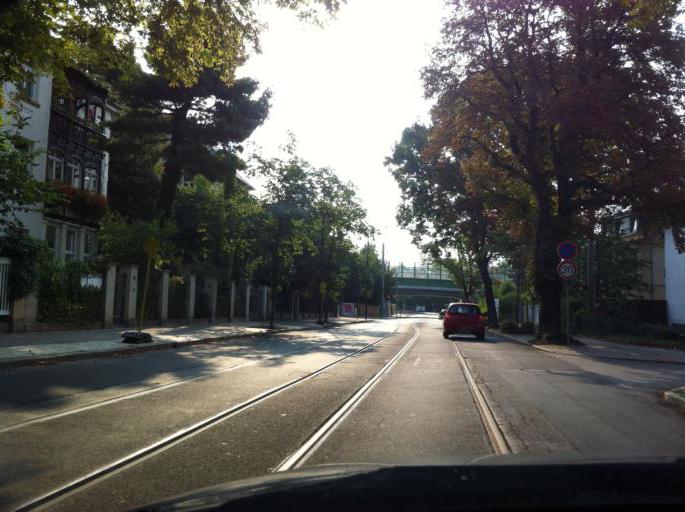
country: DE
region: Saxony
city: Markkleeberg
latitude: 51.2886
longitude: 12.3704
